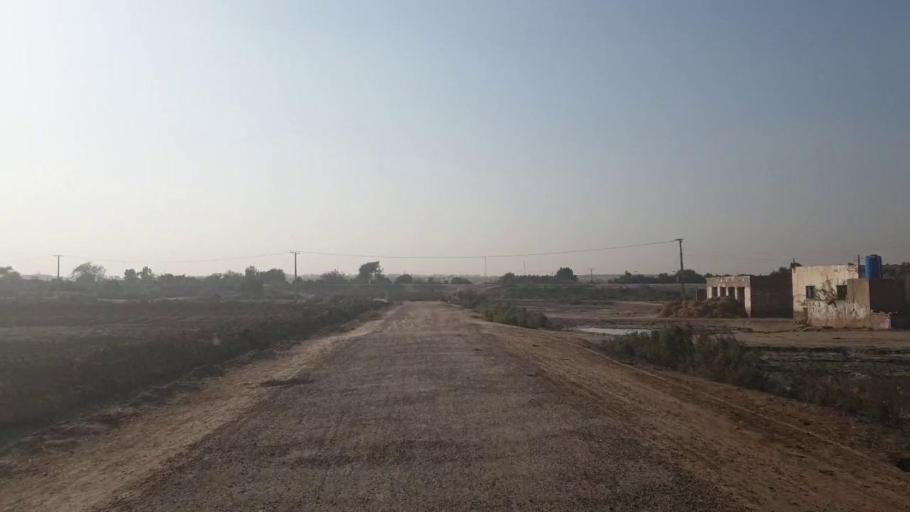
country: PK
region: Sindh
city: Kotri
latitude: 25.3940
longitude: 68.2885
